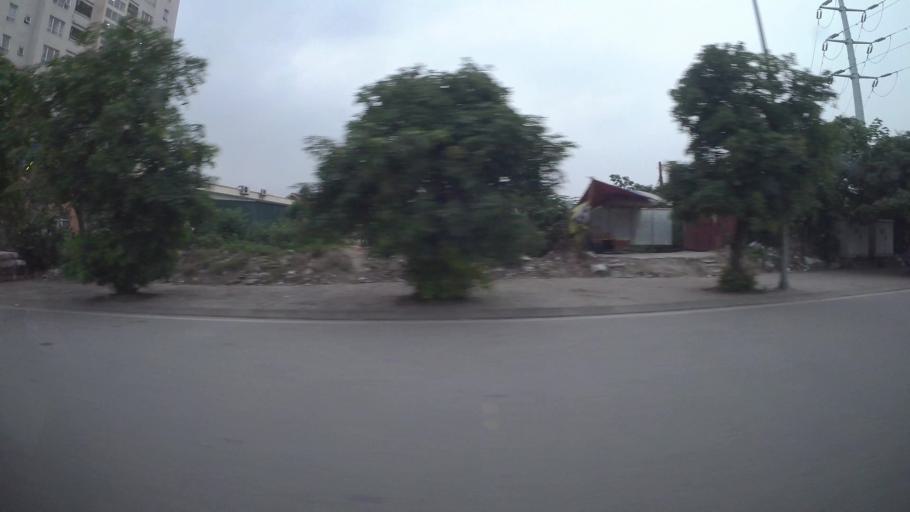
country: VN
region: Ha Noi
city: Trau Quy
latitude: 21.0403
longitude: 105.9130
